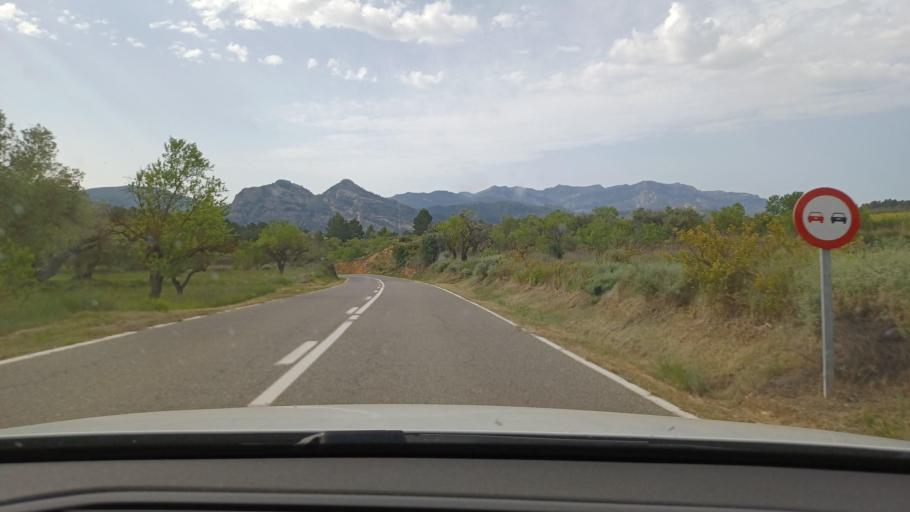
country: ES
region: Catalonia
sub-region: Provincia de Tarragona
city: Bot
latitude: 41.0241
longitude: 0.3808
